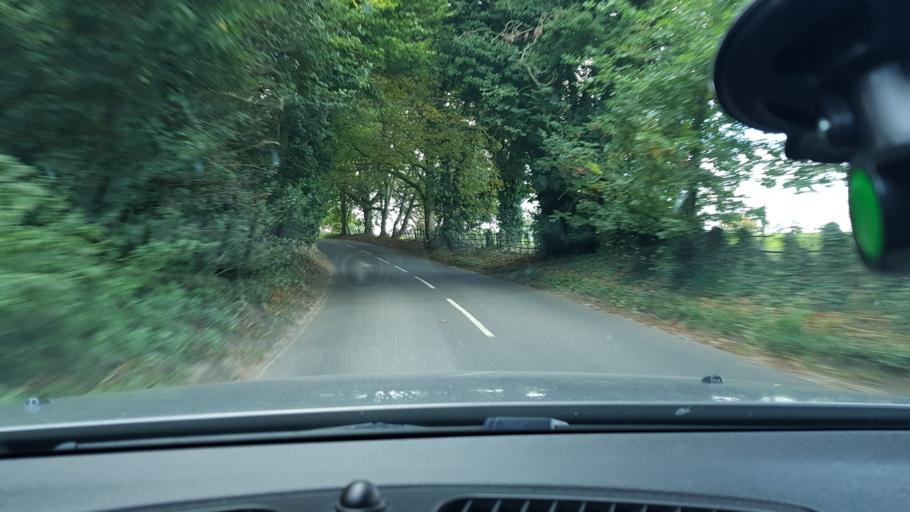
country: GB
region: England
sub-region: West Berkshire
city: Hungerford
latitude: 51.4080
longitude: -1.4837
